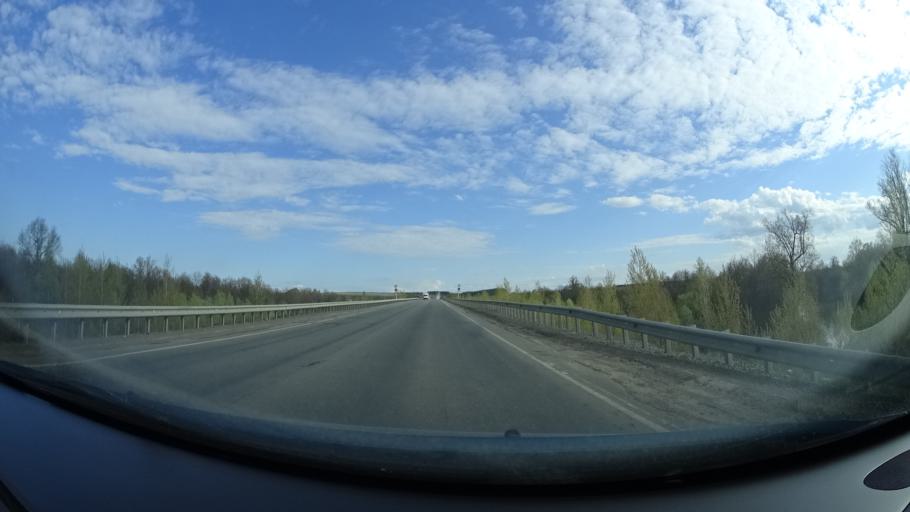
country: RU
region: Bashkortostan
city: Blagoveshchensk
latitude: 55.0629
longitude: 55.8087
